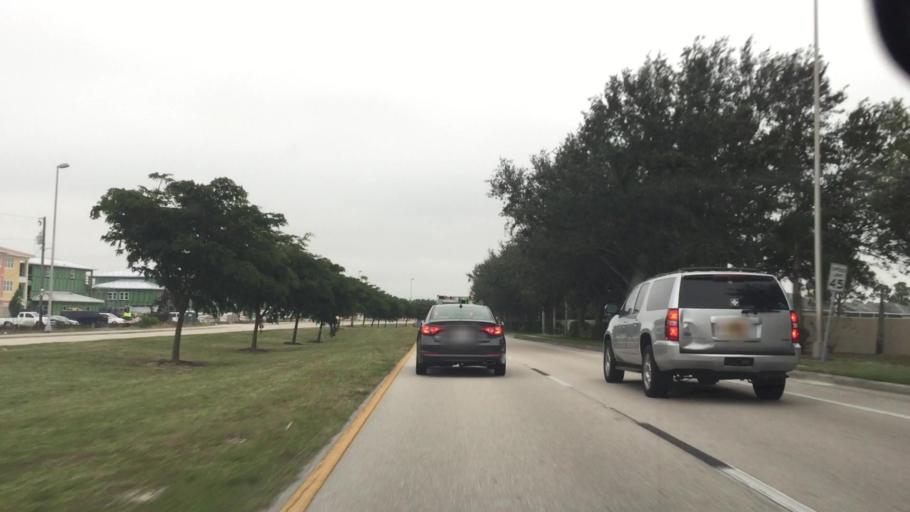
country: US
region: Florida
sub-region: Lee County
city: Three Oaks
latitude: 26.4810
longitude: -81.7973
